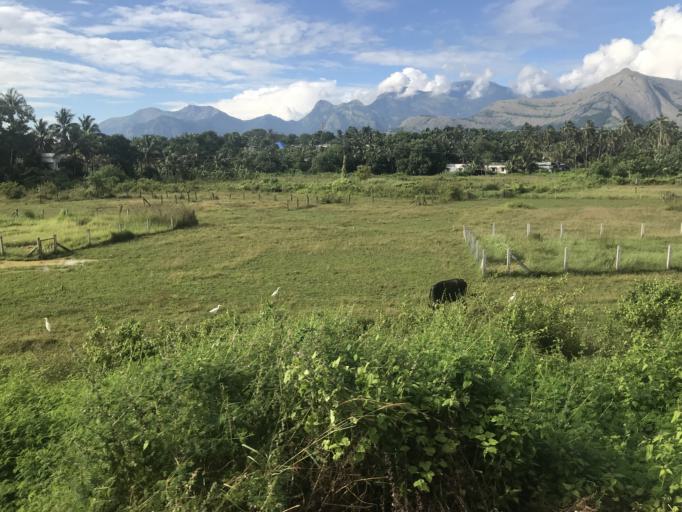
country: IN
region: Kerala
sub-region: Palakkad district
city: Palakkad
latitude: 10.8074
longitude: 76.6523
